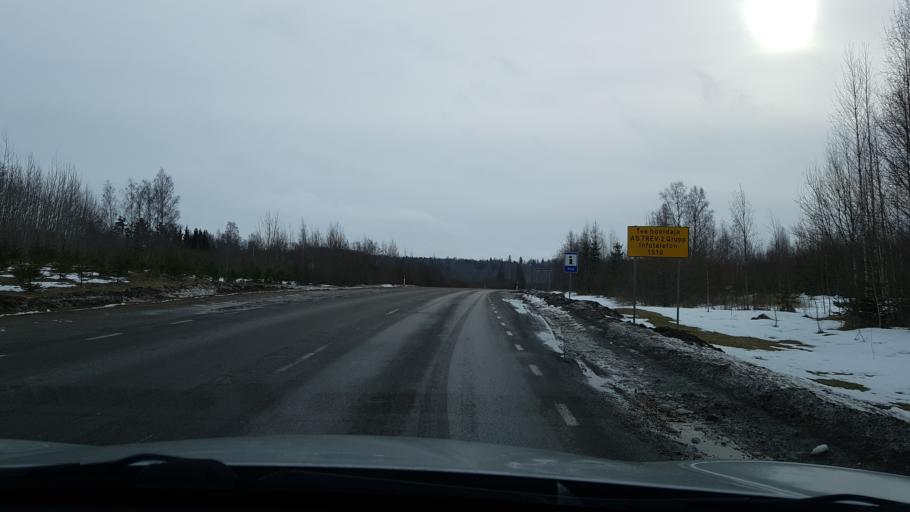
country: EE
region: Tartu
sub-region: Noo vald
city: Noo
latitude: 58.1643
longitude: 26.5491
